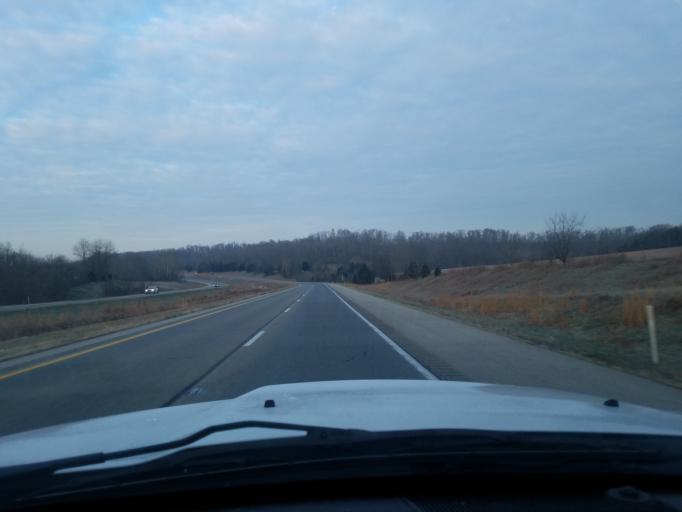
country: US
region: Indiana
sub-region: Harrison County
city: Corydon
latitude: 38.2428
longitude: -86.2002
